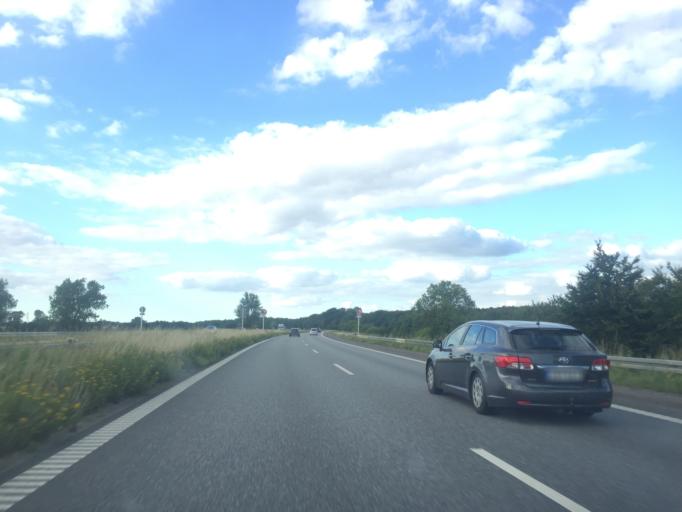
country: DK
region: Zealand
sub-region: Koge Kommune
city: Bjaeverskov
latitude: 55.3995
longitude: 12.0962
